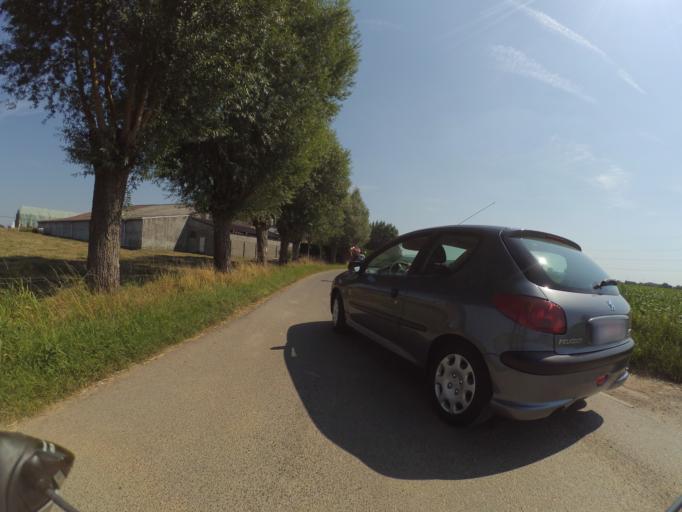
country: BE
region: Flanders
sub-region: Provincie West-Vlaanderen
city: Avelgem
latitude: 50.7933
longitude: 3.4603
